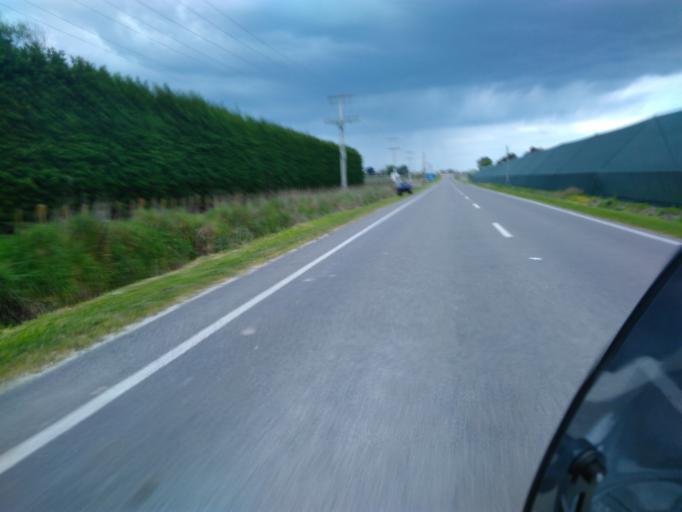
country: NZ
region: Gisborne
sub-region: Gisborne District
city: Gisborne
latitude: -38.6498
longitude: 177.9111
